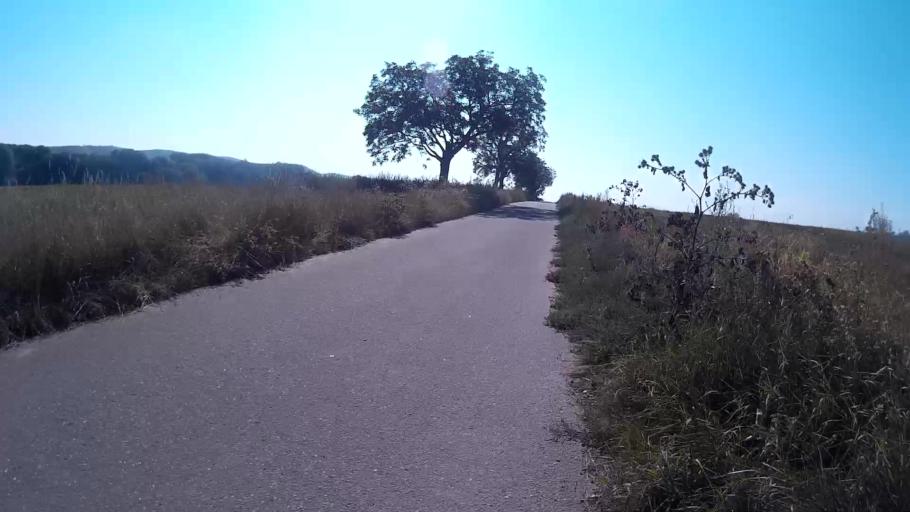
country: CZ
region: South Moravian
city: Novosedly
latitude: 48.8584
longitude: 16.5354
